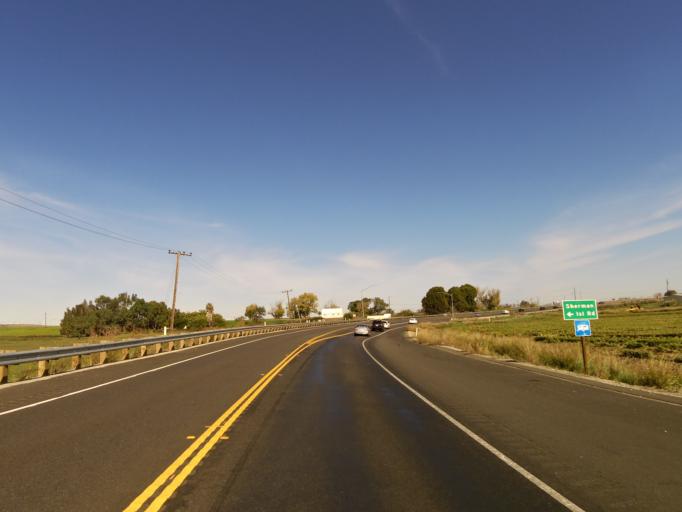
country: US
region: California
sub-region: Contra Costa County
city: Oakley
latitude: 38.0777
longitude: -121.7330
